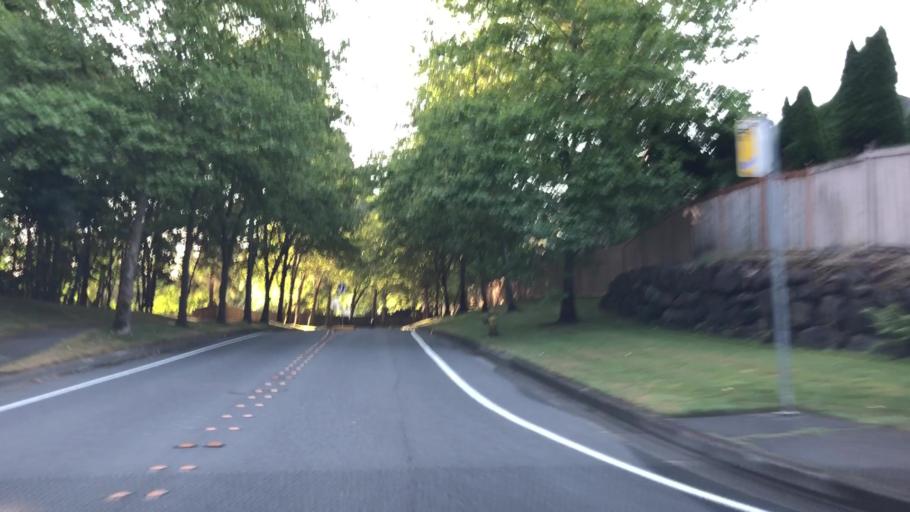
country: US
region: Washington
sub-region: King County
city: Redmond
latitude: 47.6946
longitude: -122.1034
